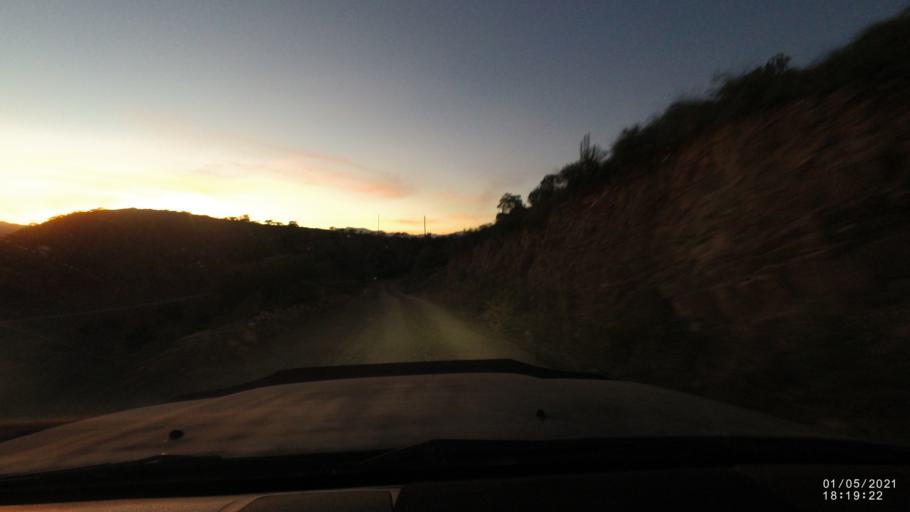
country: BO
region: Cochabamba
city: Capinota
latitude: -17.6624
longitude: -66.2246
